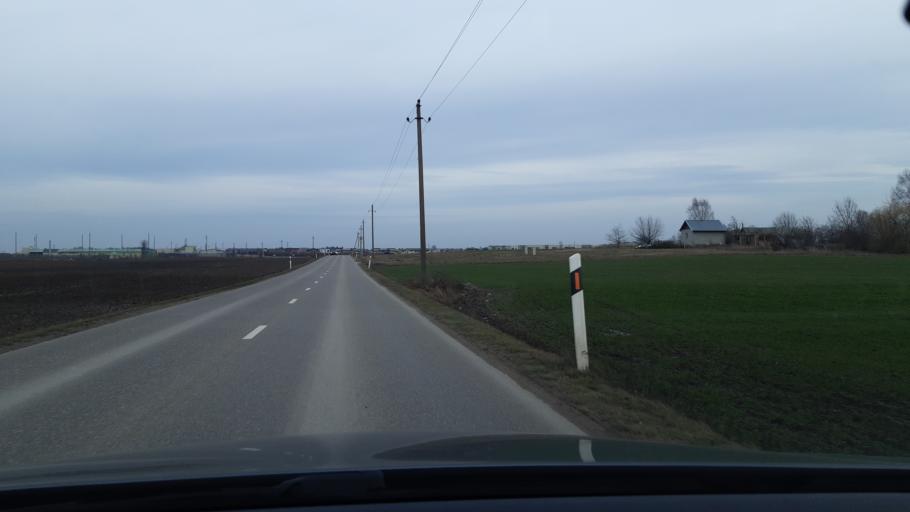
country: LT
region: Kauno apskritis
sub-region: Kaunas
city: Sargenai
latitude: 54.9489
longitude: 23.8382
